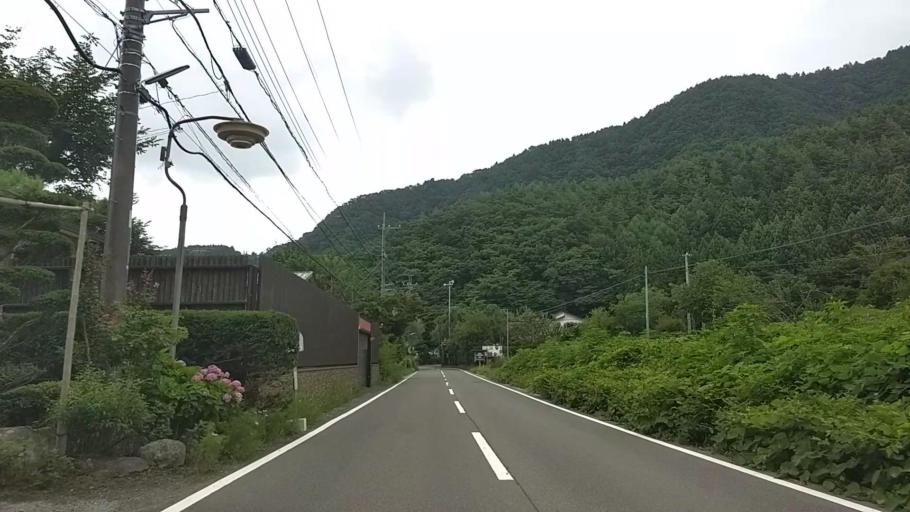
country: JP
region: Yamanashi
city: Fujikawaguchiko
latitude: 35.5029
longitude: 138.7204
